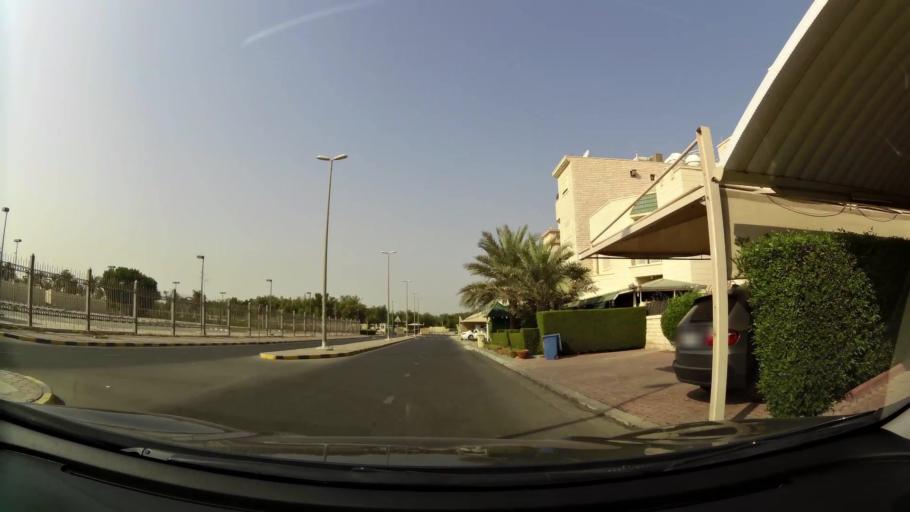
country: KW
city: Bayan
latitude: 29.2883
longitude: 48.0475
